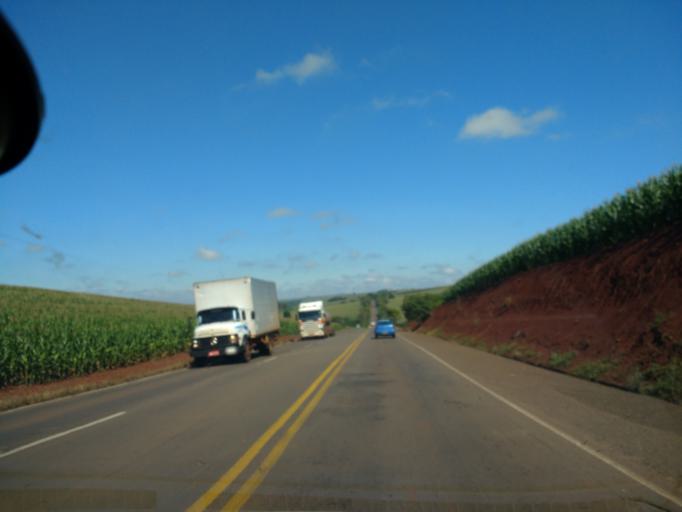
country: BR
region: Parana
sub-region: Terra Boa
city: Terra Boa
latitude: -23.6117
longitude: -52.4244
